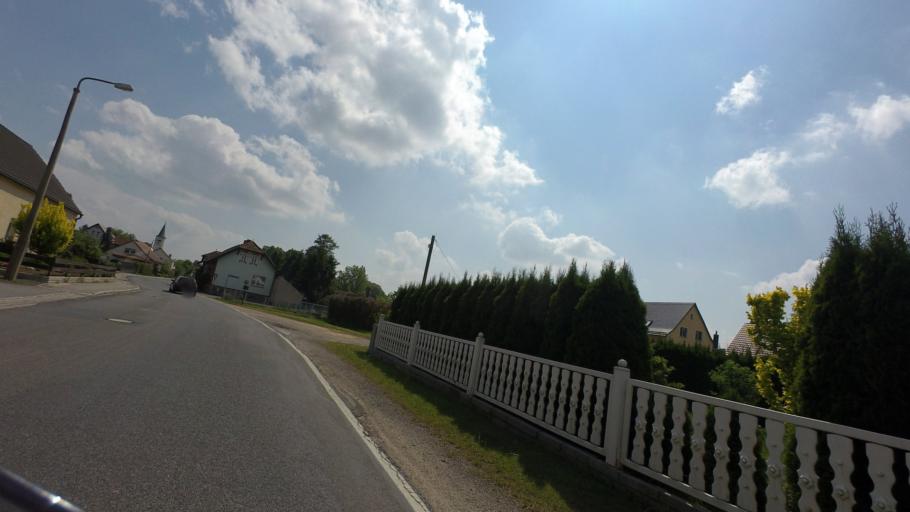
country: DE
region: Saxony
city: Weissenberg
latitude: 51.2673
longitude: 14.6454
